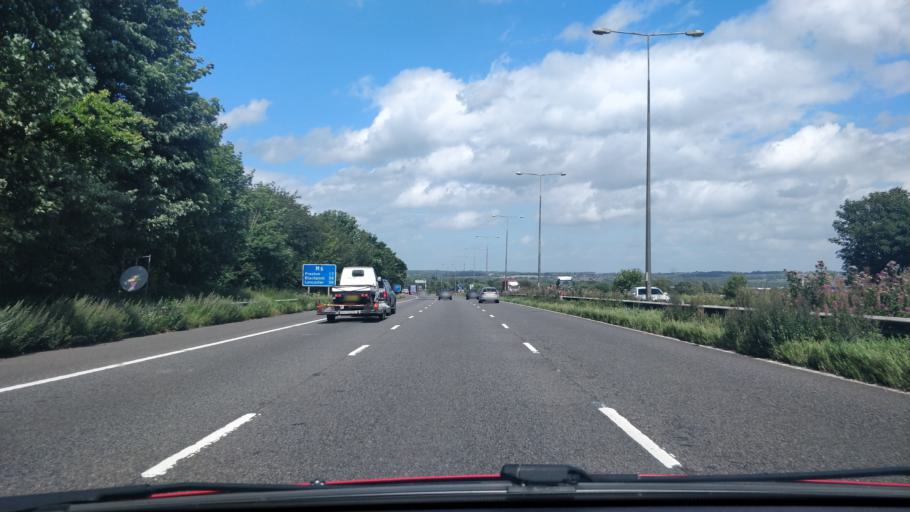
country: GB
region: England
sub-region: Borough of Wigan
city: Shevington
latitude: 53.5396
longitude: -2.6972
